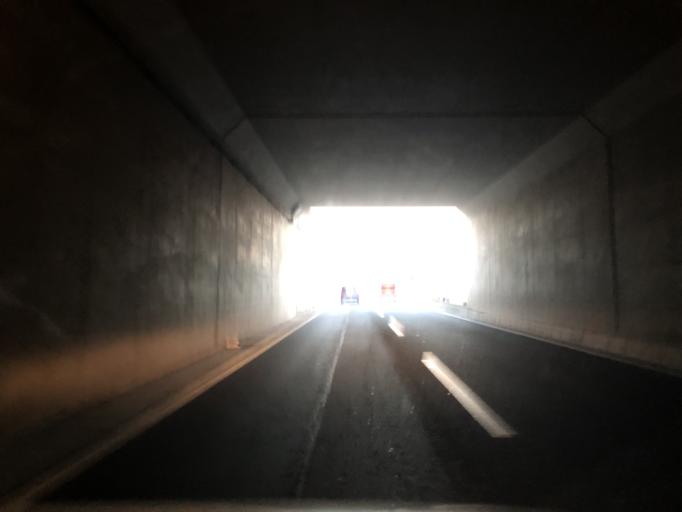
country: JP
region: Saitama
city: Sakado
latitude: 36.0232
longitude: 139.4135
